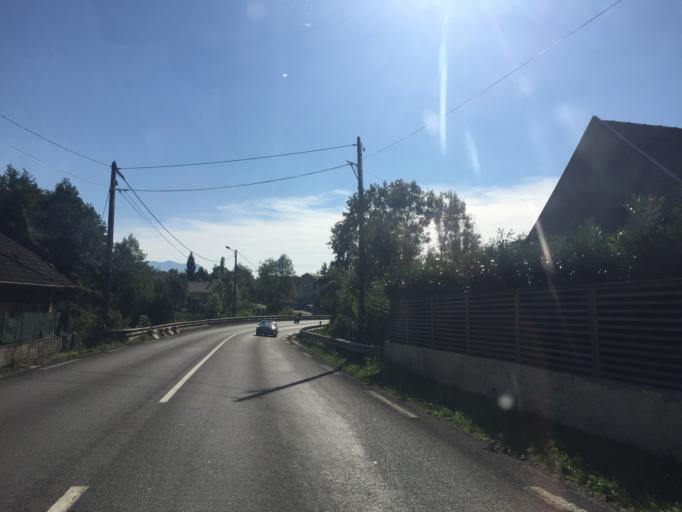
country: FR
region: Rhone-Alpes
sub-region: Departement de la Haute-Savoie
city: Viuz-la-Chiesaz
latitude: 45.8372
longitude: 6.0588
